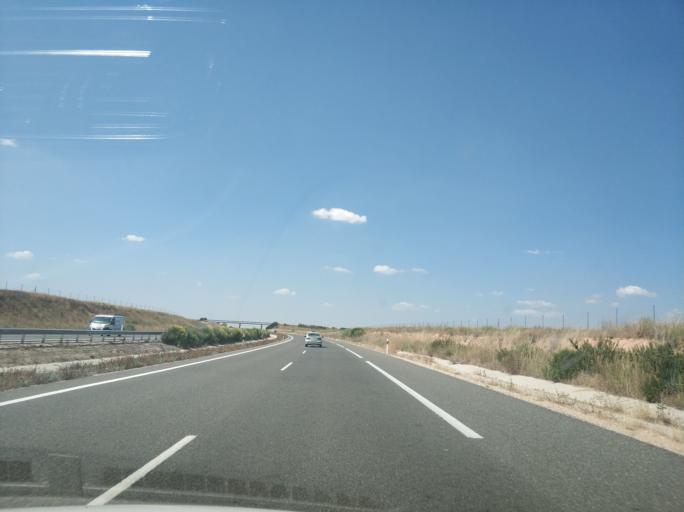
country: ES
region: Castille and Leon
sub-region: Provincia de Salamanca
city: Castellanos de Villiquera
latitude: 41.0465
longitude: -5.6673
